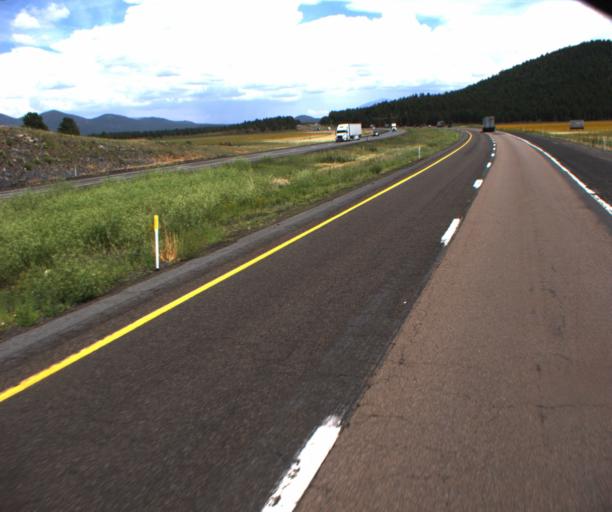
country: US
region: Arizona
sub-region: Coconino County
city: Williams
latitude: 35.2578
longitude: -112.0833
